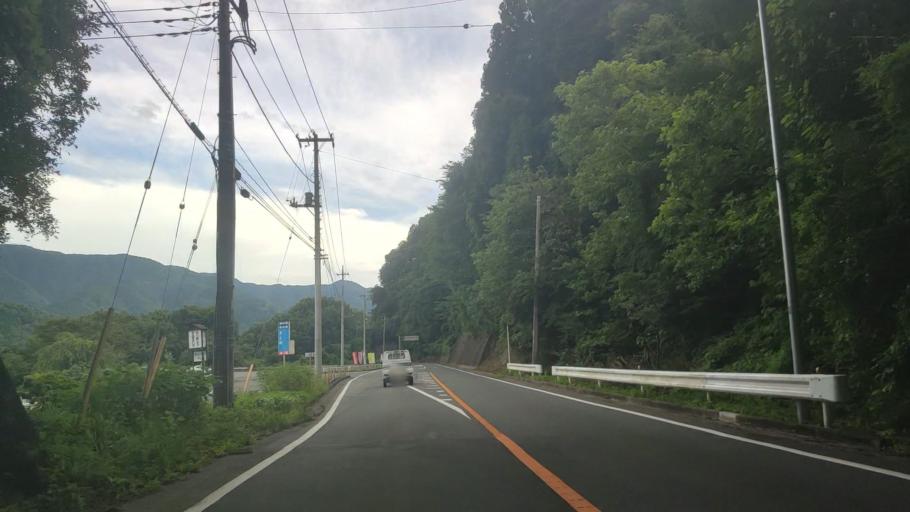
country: JP
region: Gunma
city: Omamacho-omama
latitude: 36.5496
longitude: 139.3723
